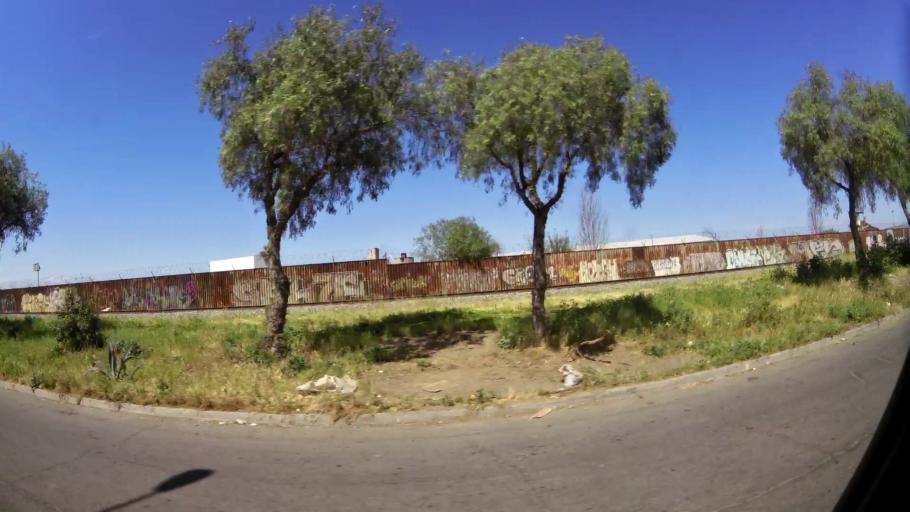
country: CL
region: Santiago Metropolitan
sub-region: Provincia de Santiago
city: Lo Prado
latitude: -33.5176
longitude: -70.7461
